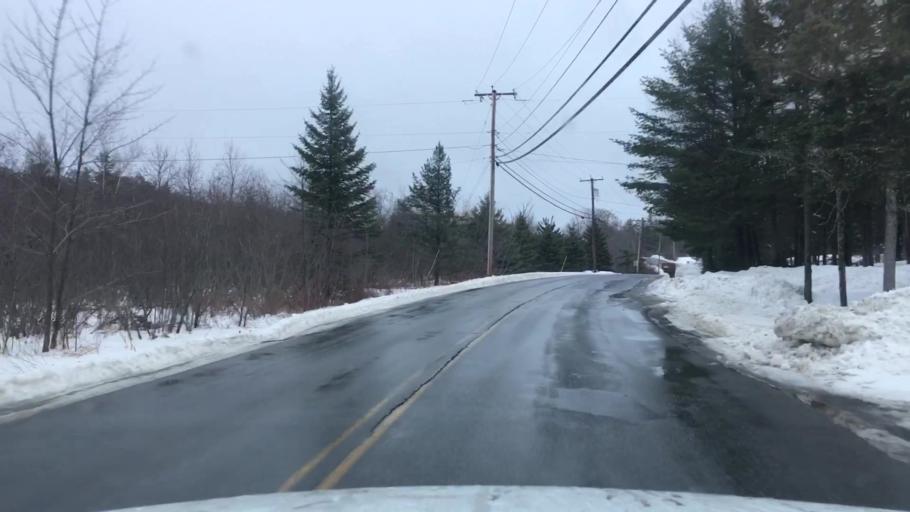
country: US
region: Maine
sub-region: Hancock County
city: Trenton
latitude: 44.4150
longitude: -68.2891
